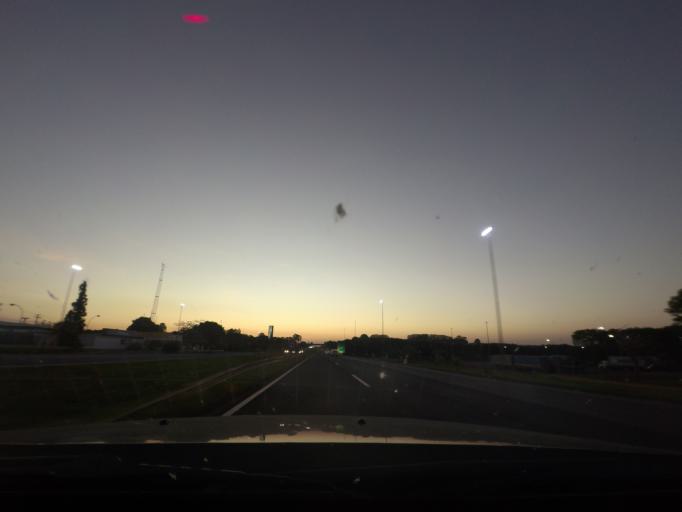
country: BR
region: Sao Paulo
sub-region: Piracicaba
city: Piracicaba
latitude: -22.7223
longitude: -47.5993
